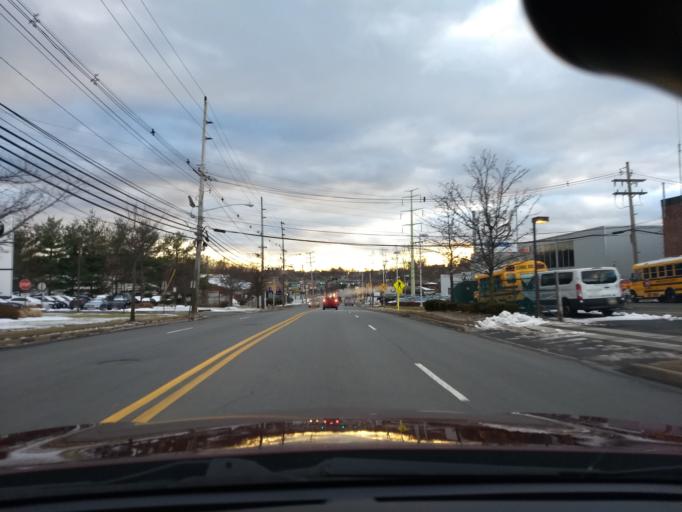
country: US
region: New Jersey
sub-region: Morris County
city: Morristown
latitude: 40.8030
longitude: -74.4649
